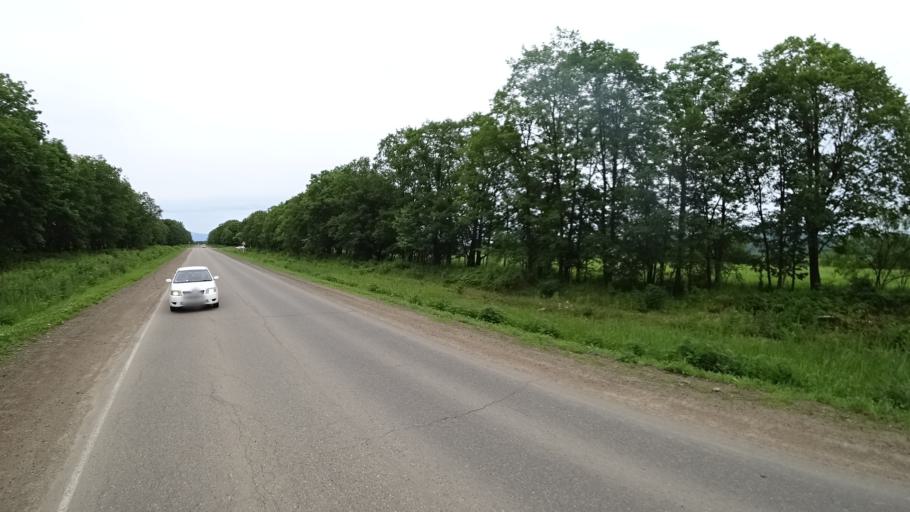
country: RU
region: Primorskiy
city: Novosysoyevka
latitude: 44.1900
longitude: 133.3546
